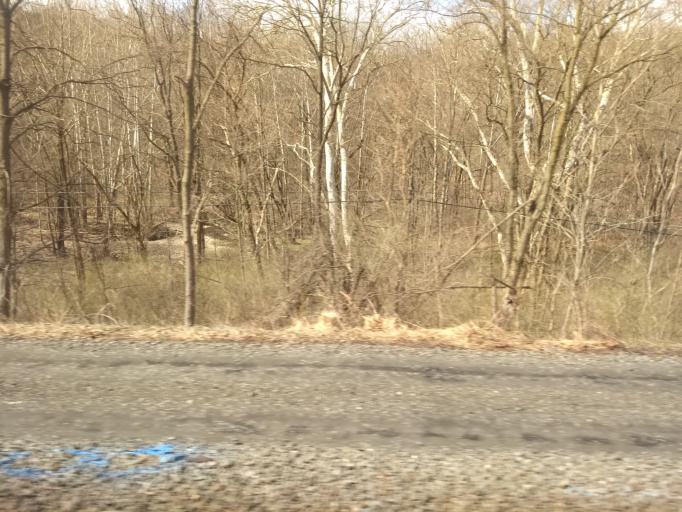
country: US
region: Pennsylvania
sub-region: Blair County
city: Tyrone
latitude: 40.6252
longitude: -78.1705
